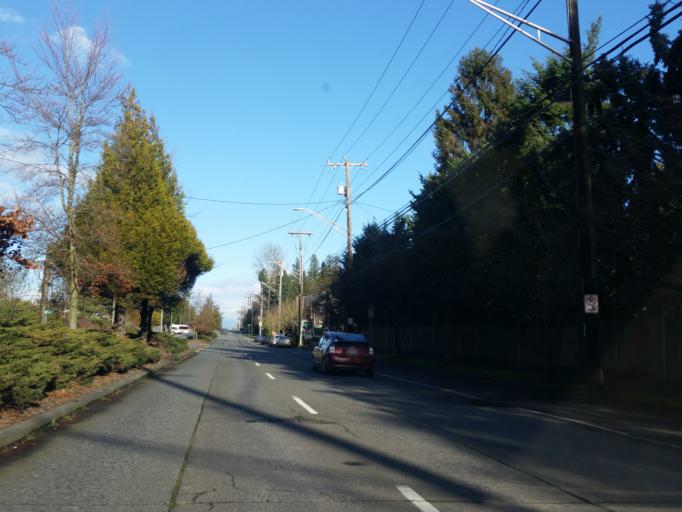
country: US
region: Washington
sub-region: King County
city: Yarrow Point
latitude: 47.6703
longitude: -122.2708
